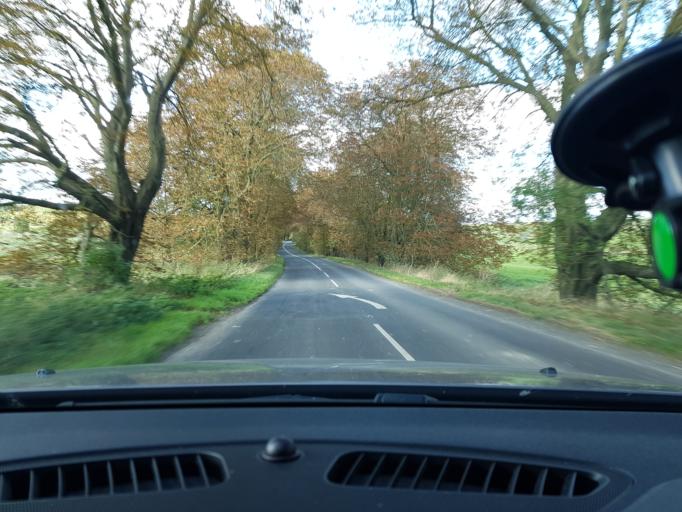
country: GB
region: England
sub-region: Borough of Swindon
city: Wanborough
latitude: 51.5142
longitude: -1.6794
